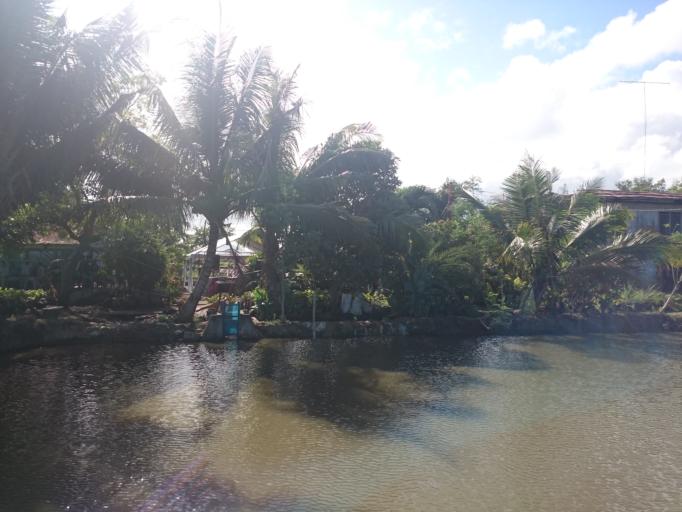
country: PH
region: Central Visayas
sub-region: Province of Negros Oriental
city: Tanjay
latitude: 9.5002
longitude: 123.1546
